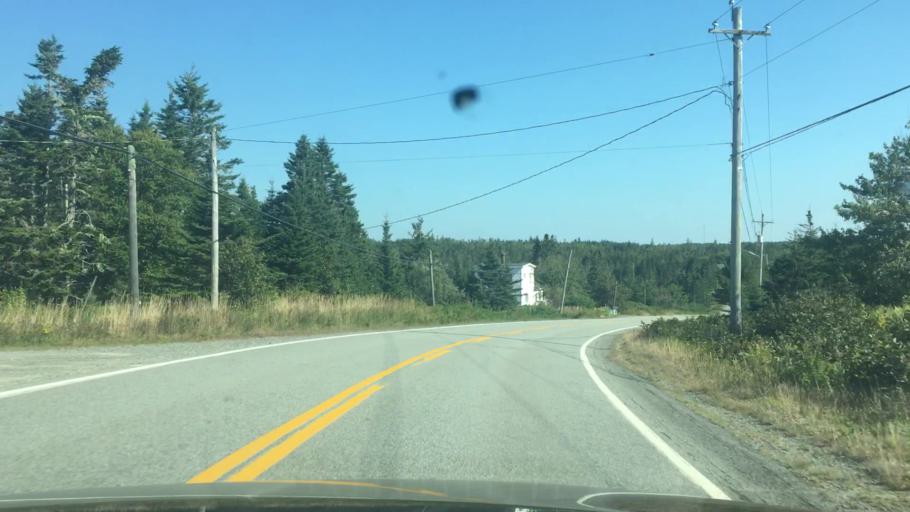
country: CA
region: Nova Scotia
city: Cole Harbour
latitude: 44.7990
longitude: -62.7161
